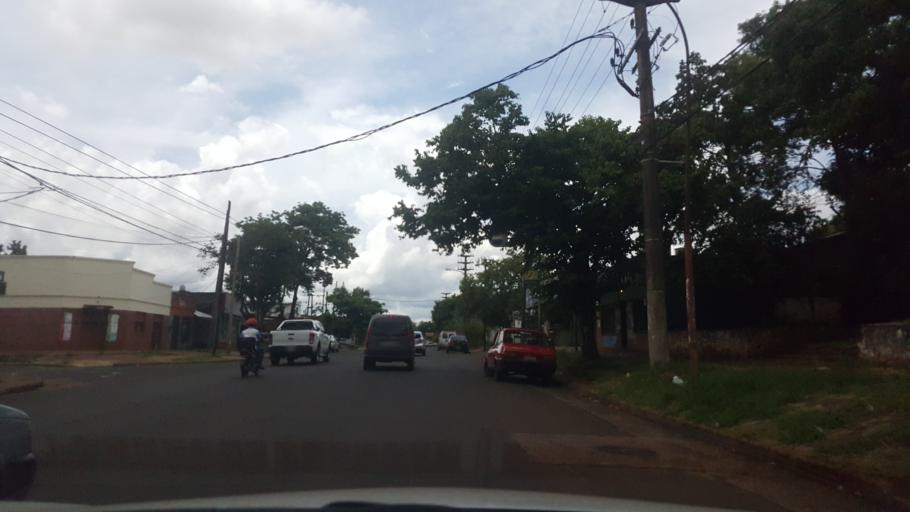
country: AR
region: Misiones
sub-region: Departamento de Capital
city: Posadas
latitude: -27.3931
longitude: -55.8973
